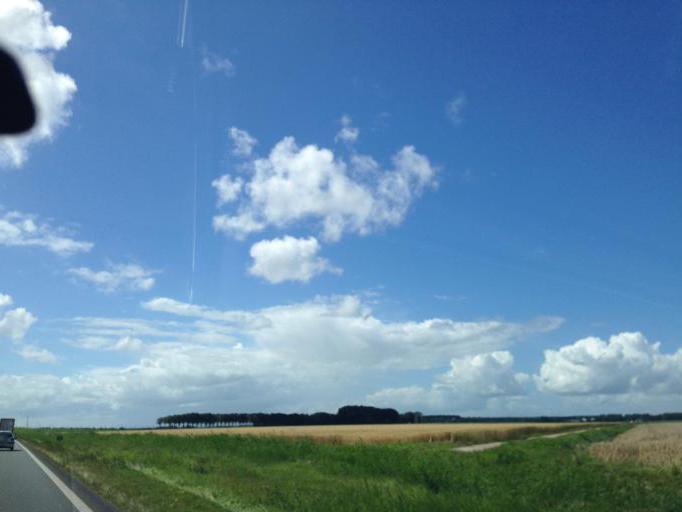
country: NL
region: Flevoland
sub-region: Gemeente Dronten
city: Dronten
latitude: 52.5498
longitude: 5.6820
